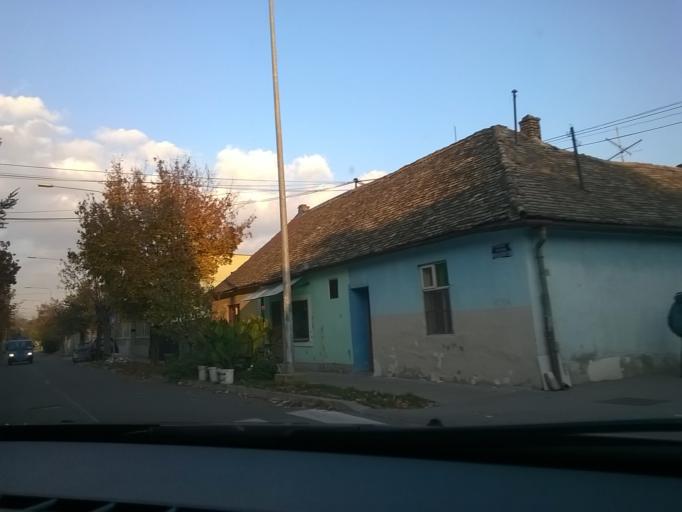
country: RS
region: Autonomna Pokrajina Vojvodina
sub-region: Juznobanatski Okrug
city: Pancevo
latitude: 44.8646
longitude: 20.6476
